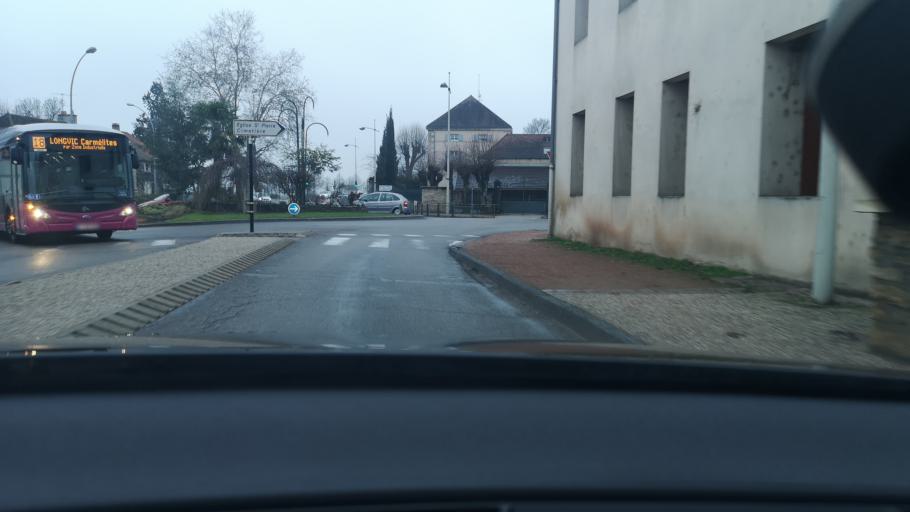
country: FR
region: Bourgogne
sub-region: Departement de la Cote-d'Or
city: Longvic
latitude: 47.2839
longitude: 5.0629
